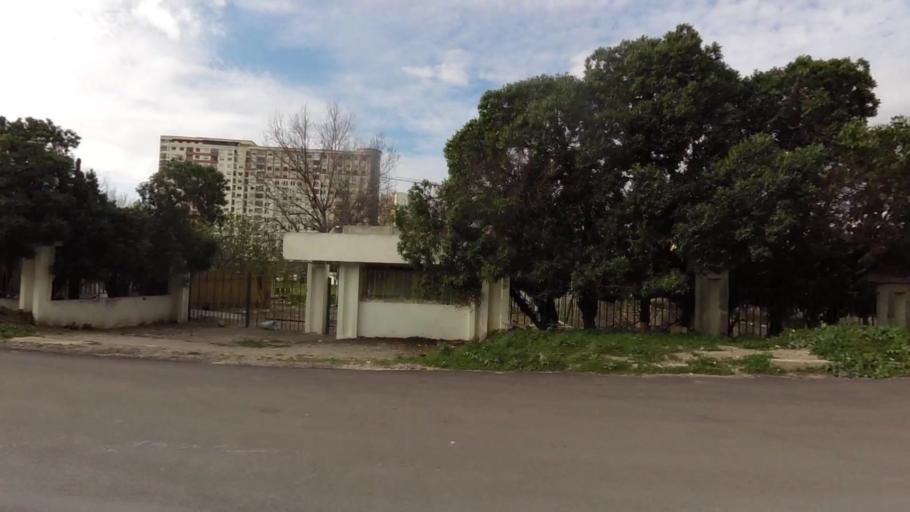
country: MA
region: Tanger-Tetouan
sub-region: Tanger-Assilah
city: Tangier
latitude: 35.7705
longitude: -5.7912
